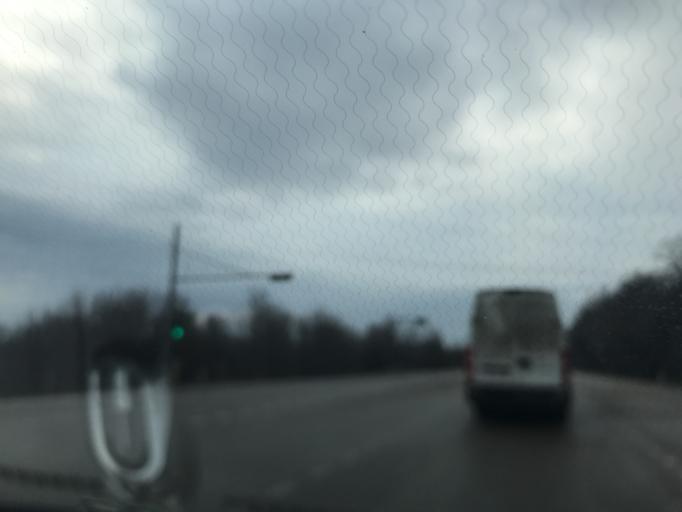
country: RU
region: Krasnodarskiy
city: Tikhoretsk
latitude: 45.8807
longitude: 40.1359
